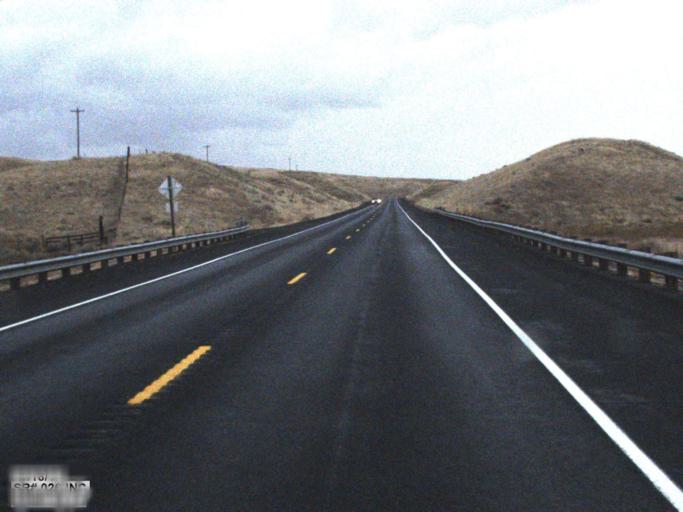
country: US
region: Washington
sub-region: Columbia County
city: Dayton
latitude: 46.7651
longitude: -118.0165
